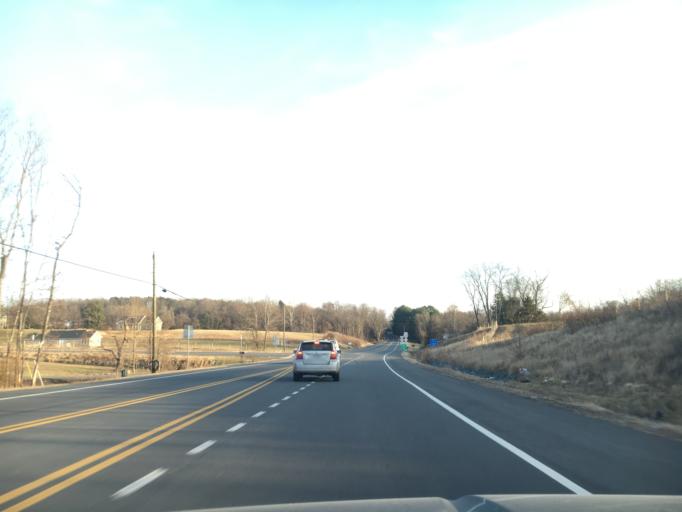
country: US
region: Virginia
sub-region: Culpeper County
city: Culpeper
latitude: 38.4908
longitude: -78.0300
